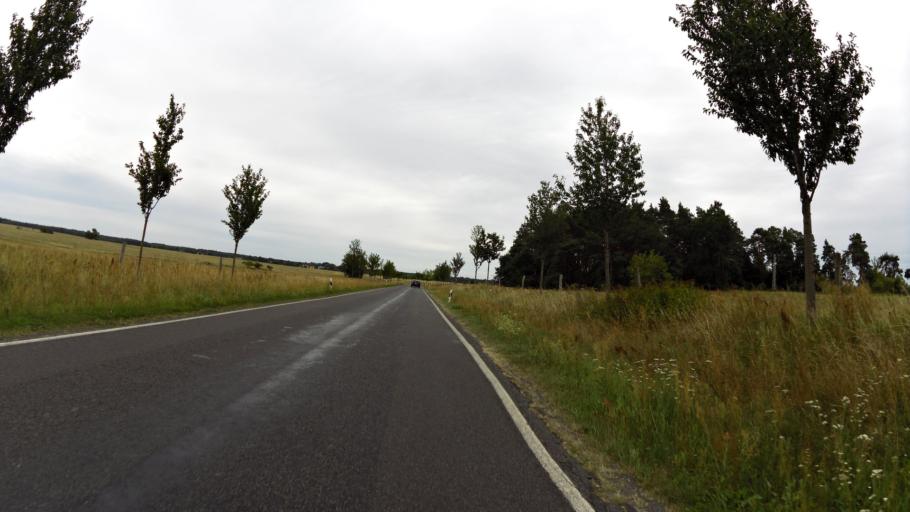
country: DE
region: Brandenburg
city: Wendisch Rietz
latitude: 52.1818
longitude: 14.0589
